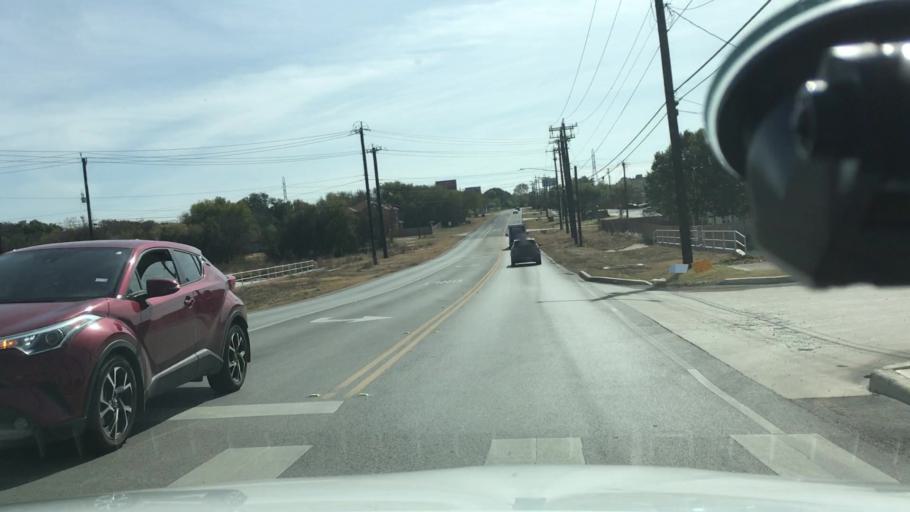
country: US
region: Texas
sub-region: Bexar County
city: Hollywood Park
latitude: 29.5790
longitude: -98.4203
